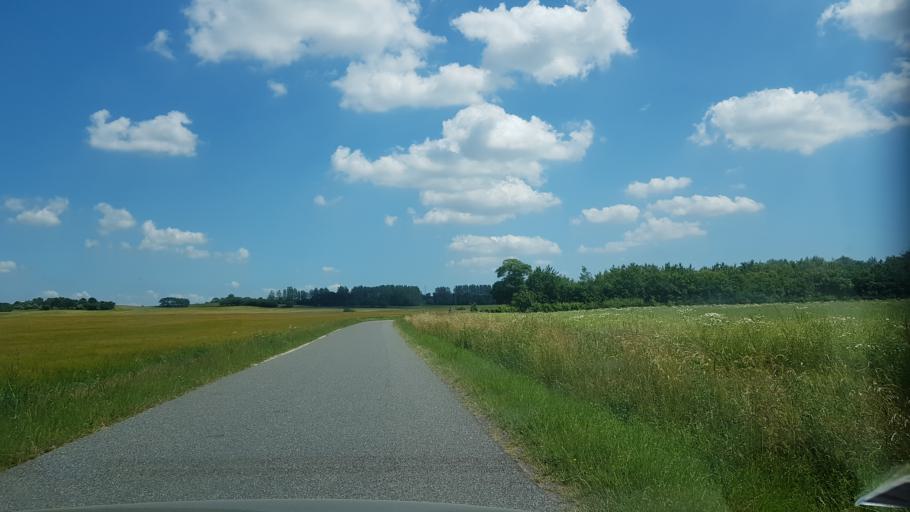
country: DK
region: Zealand
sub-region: Kalundborg Kommune
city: Svebolle
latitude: 55.7019
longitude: 11.2898
